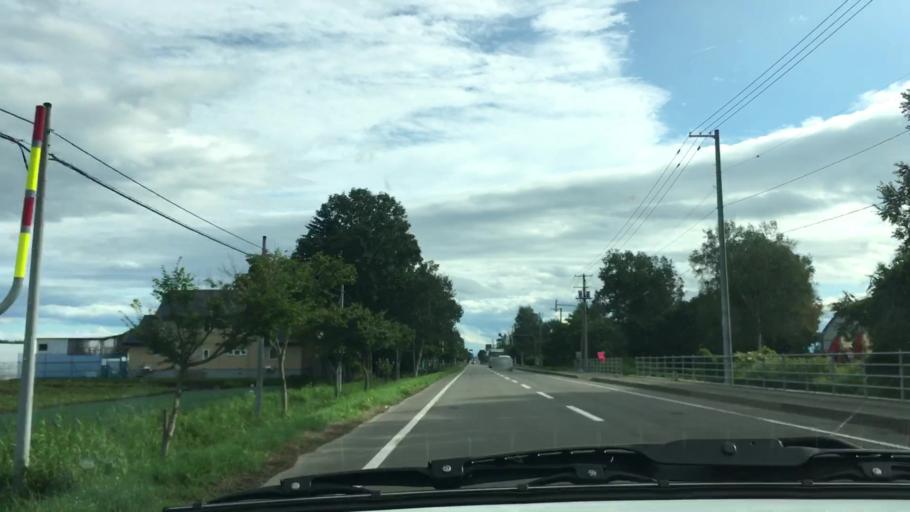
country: JP
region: Hokkaido
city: Otofuke
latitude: 43.2435
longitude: 143.2975
